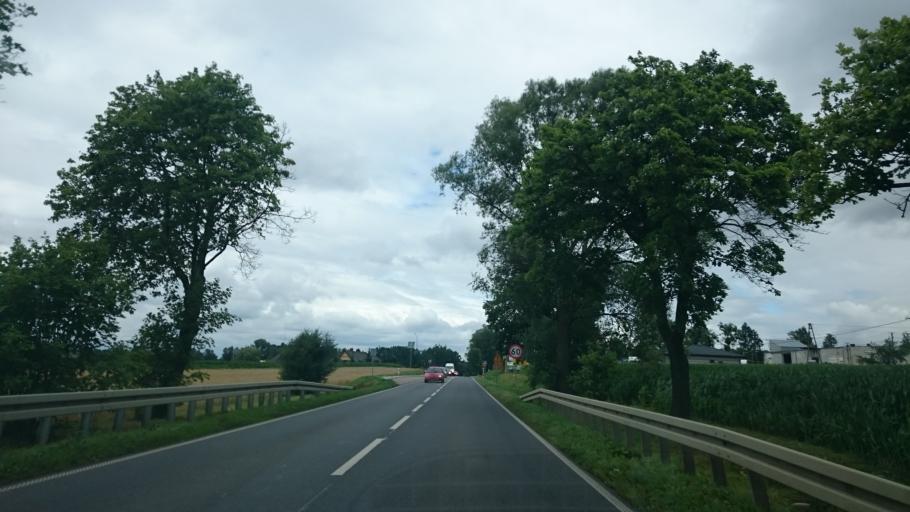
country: PL
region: Kujawsko-Pomorskie
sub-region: Powiat rypinski
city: Rypin
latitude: 53.1146
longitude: 19.3864
